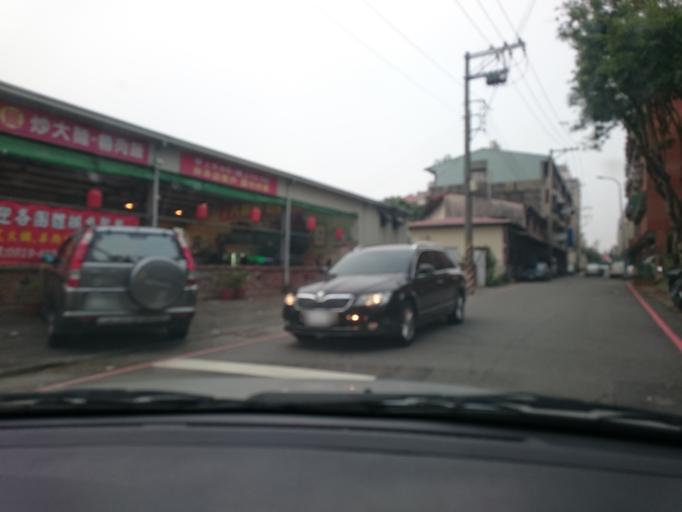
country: TW
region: Taiwan
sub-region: Taichung City
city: Taichung
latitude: 24.1728
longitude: 120.6381
